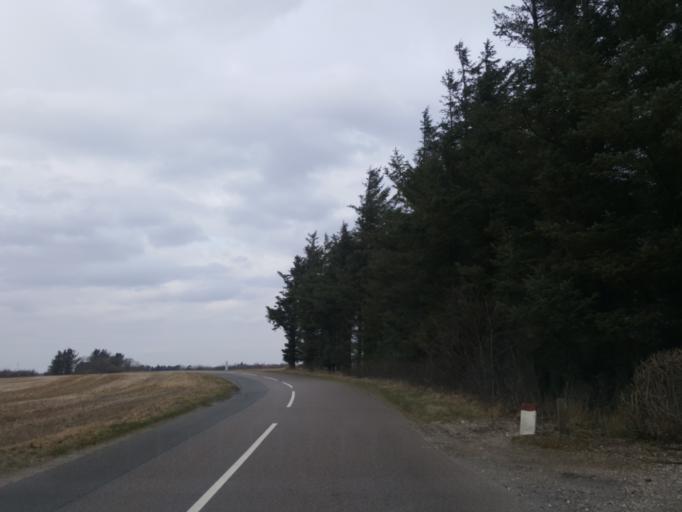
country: DK
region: Central Jutland
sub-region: Lemvig Kommune
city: Lemvig
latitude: 56.4148
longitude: 8.2342
